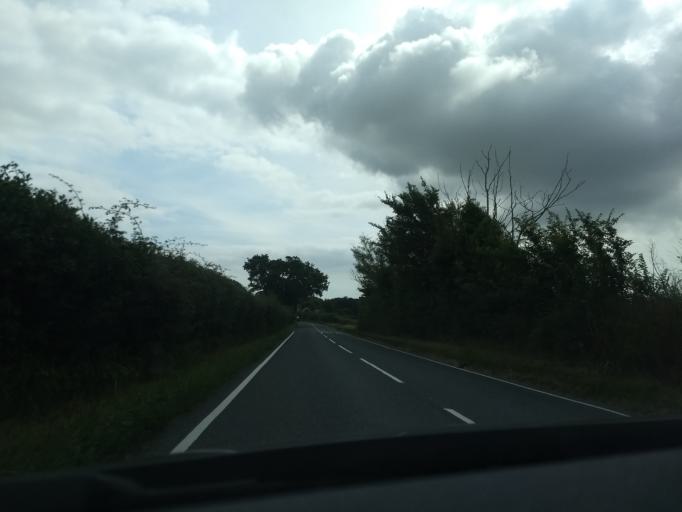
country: GB
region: England
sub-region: Suffolk
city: Ipswich
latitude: 52.0053
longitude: 1.1674
